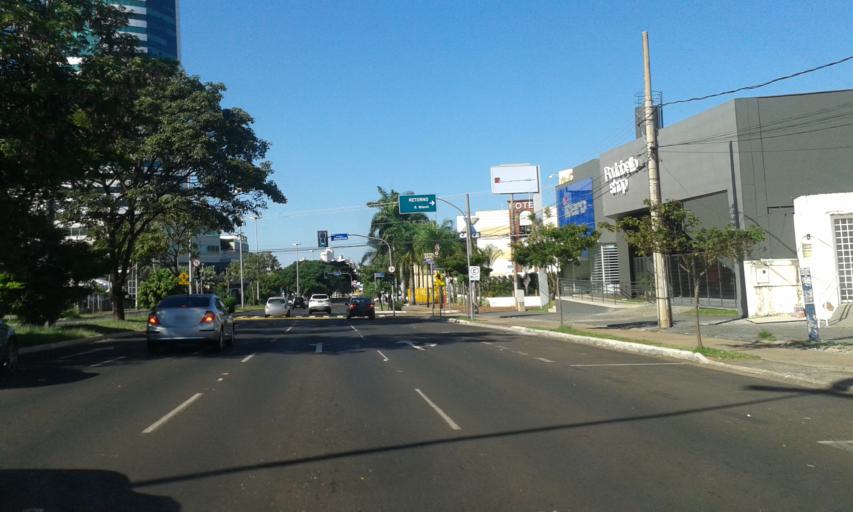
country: BR
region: Minas Gerais
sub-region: Uberlandia
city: Uberlandia
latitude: -18.9061
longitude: -48.2614
